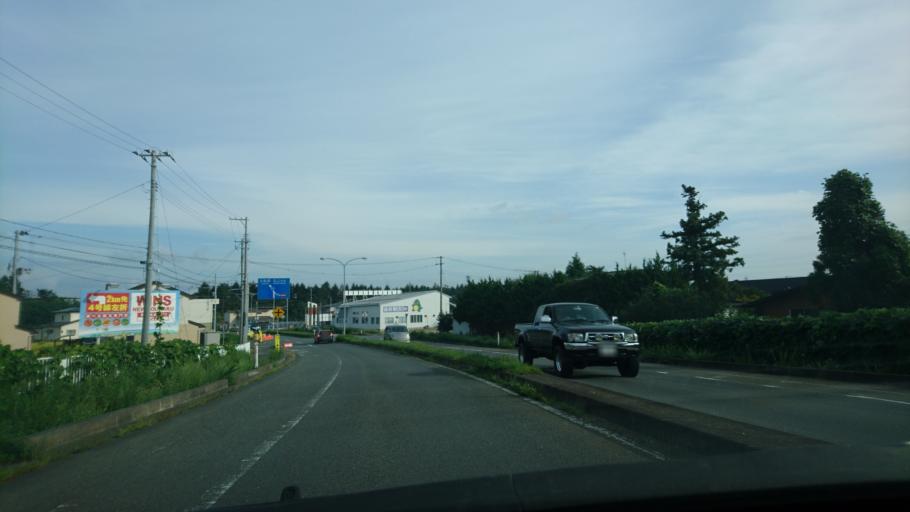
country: JP
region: Iwate
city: Kitakami
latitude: 39.2961
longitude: 141.0838
